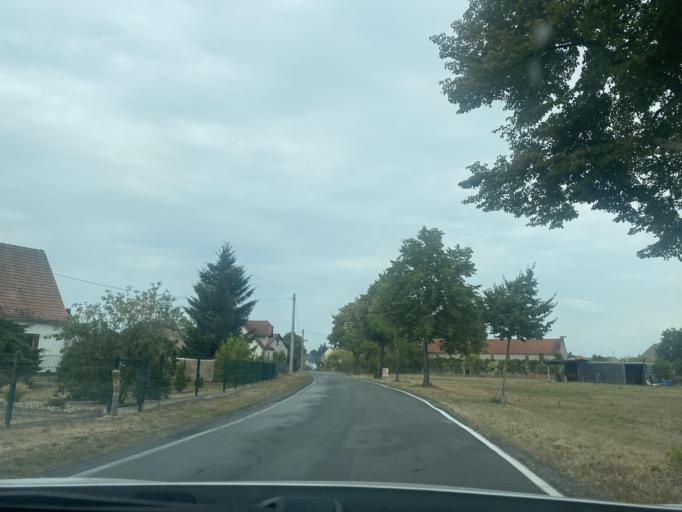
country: DE
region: Saxony
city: Wittichenau
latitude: 51.3523
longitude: 14.2831
